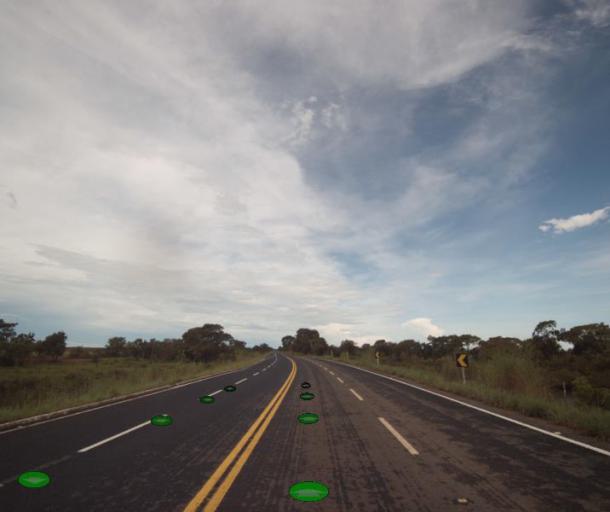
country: BR
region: Goias
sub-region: Sao Miguel Do Araguaia
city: Sao Miguel do Araguaia
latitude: -13.2339
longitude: -50.5626
